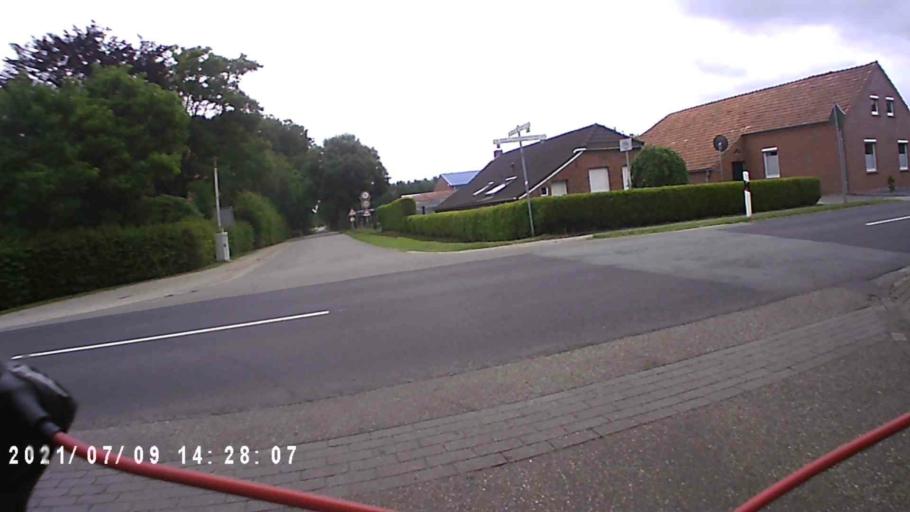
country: DE
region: Lower Saxony
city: Bunde
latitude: 53.1290
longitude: 7.2958
